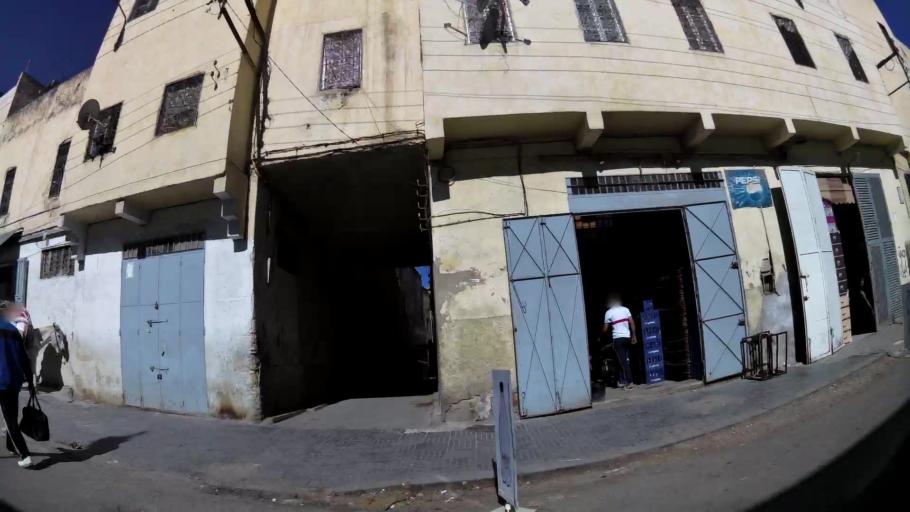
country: MA
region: Fes-Boulemane
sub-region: Fes
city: Fes
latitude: 34.0622
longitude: -4.9644
